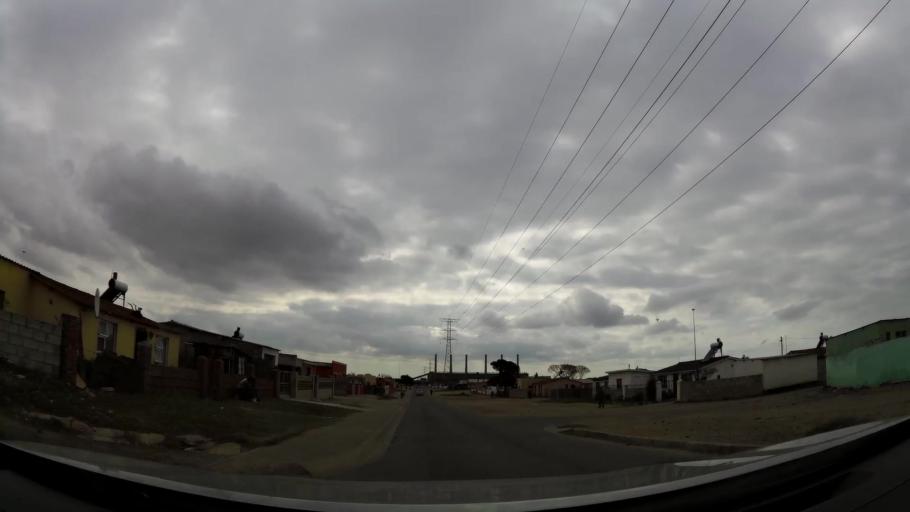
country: ZA
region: Eastern Cape
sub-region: Nelson Mandela Bay Metropolitan Municipality
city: Port Elizabeth
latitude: -33.8807
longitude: 25.5966
